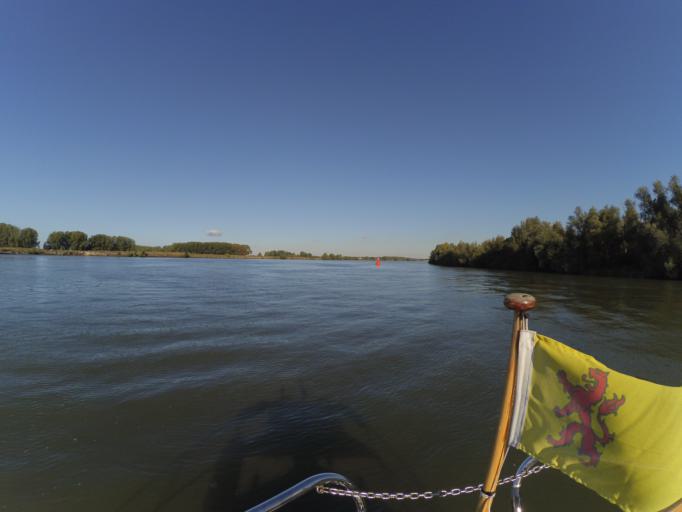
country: NL
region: South Holland
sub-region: Gemeente Zwijndrecht
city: Heerjansdam
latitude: 51.8143
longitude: 4.5658
